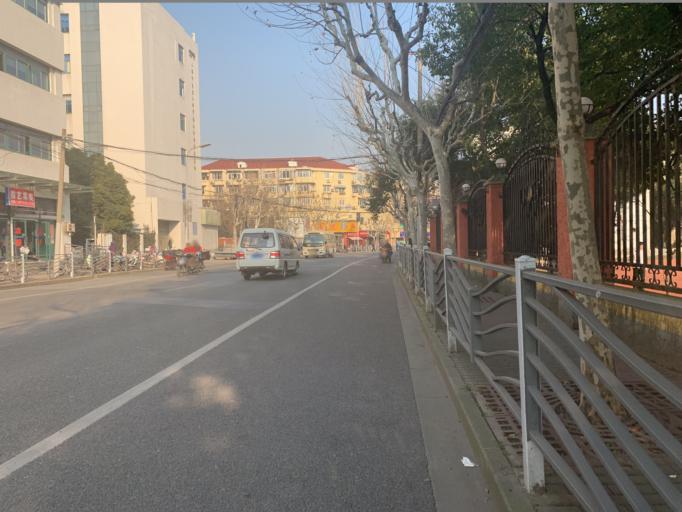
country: CN
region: Shanghai Shi
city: Changqiao
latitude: 31.1449
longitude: 121.4279
